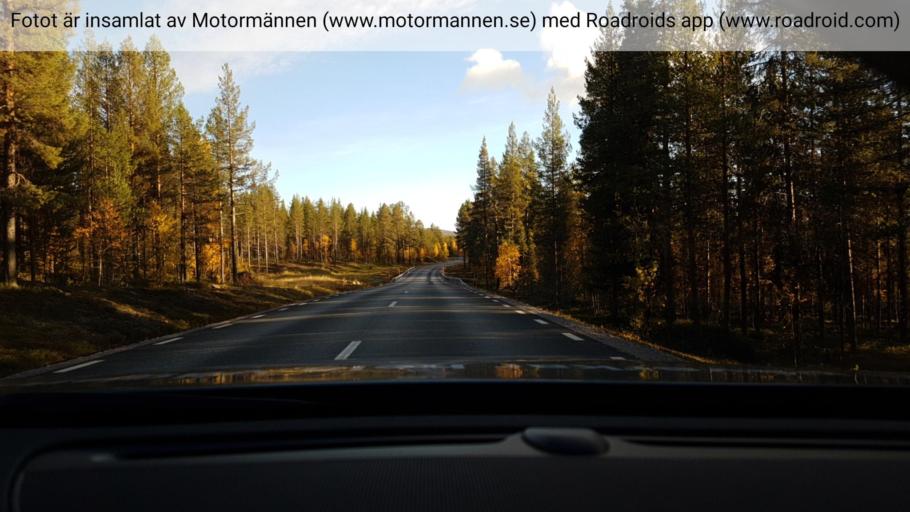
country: SE
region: Norrbotten
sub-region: Jokkmokks Kommun
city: Jokkmokk
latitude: 66.9240
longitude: 19.8263
